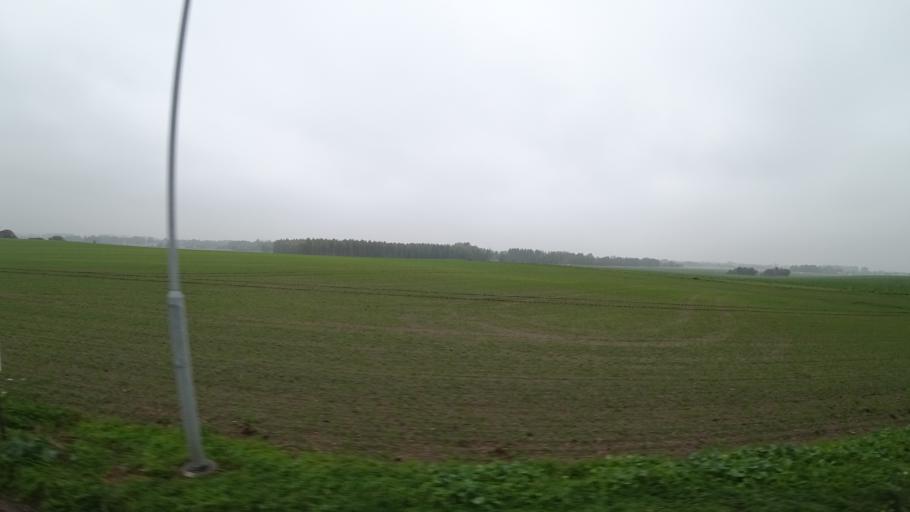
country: SE
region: Skane
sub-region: Kavlinge Kommun
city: Kaevlinge
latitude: 55.7991
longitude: 13.1638
